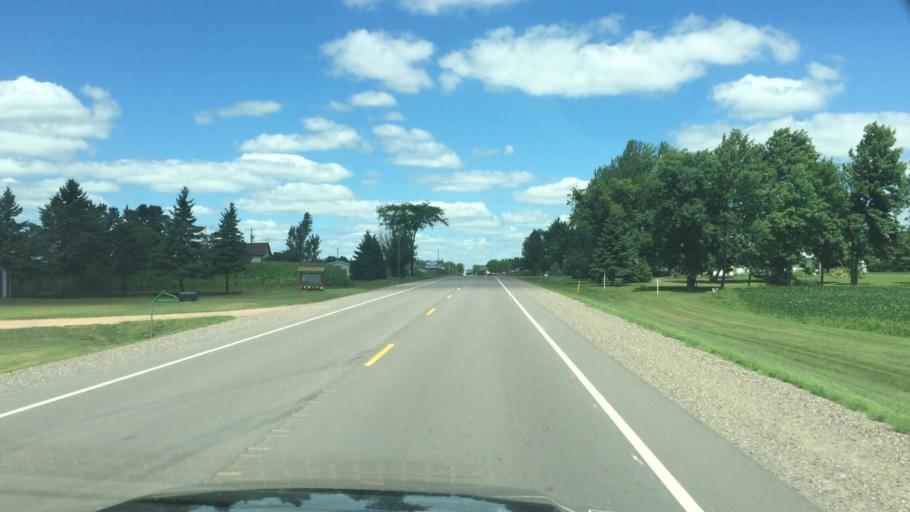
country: US
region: Wisconsin
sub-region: Clark County
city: Abbotsford
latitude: 45.0101
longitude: -90.3154
